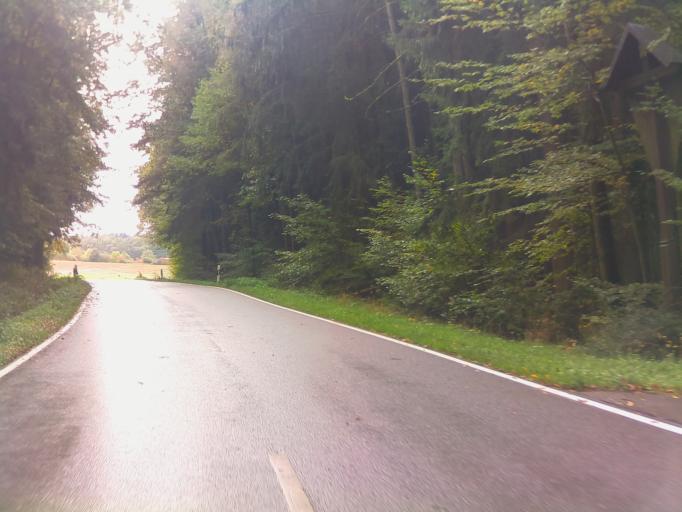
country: DE
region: Bavaria
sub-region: Upper Franconia
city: Zapfendorf
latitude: 50.0064
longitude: 10.9753
